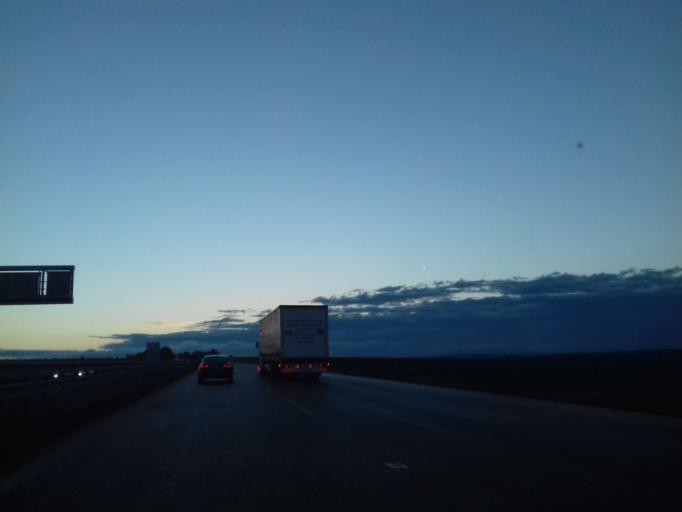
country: CZ
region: South Moravian
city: Tvarozna
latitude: 49.1828
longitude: 16.7693
